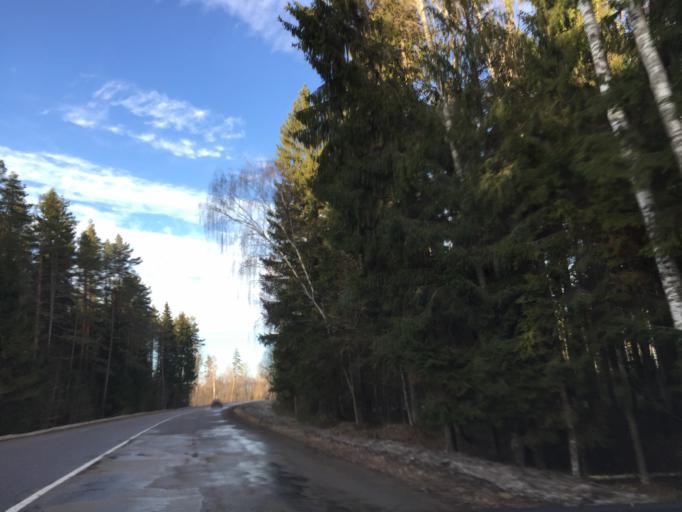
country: LV
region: Kekava
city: Balozi
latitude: 56.7608
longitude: 24.1080
